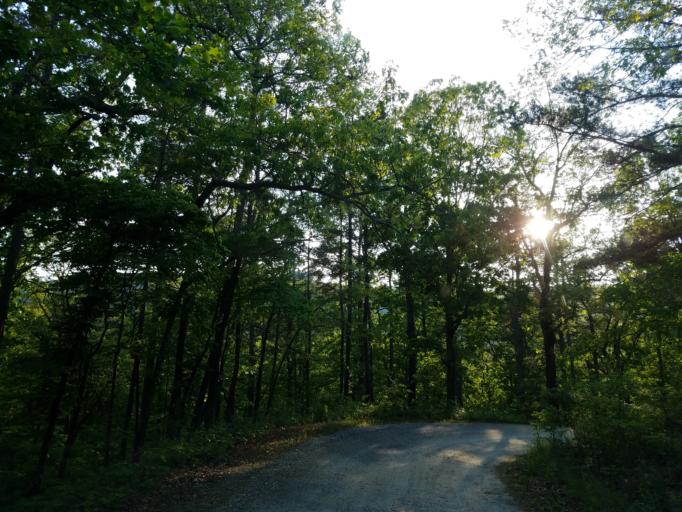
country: US
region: Georgia
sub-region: Gordon County
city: Calhoun
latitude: 34.6122
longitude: -85.0851
